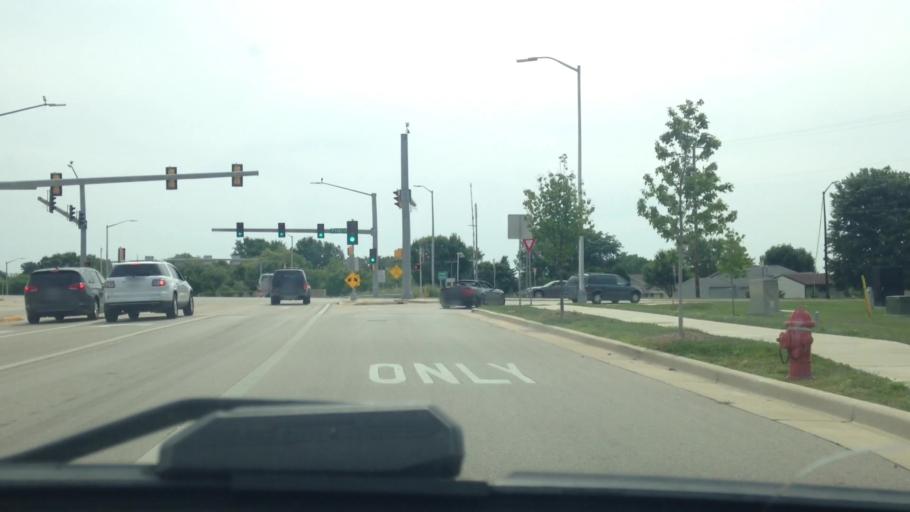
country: US
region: Wisconsin
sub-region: Waukesha County
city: Menomonee Falls
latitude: 43.1812
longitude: -88.1040
